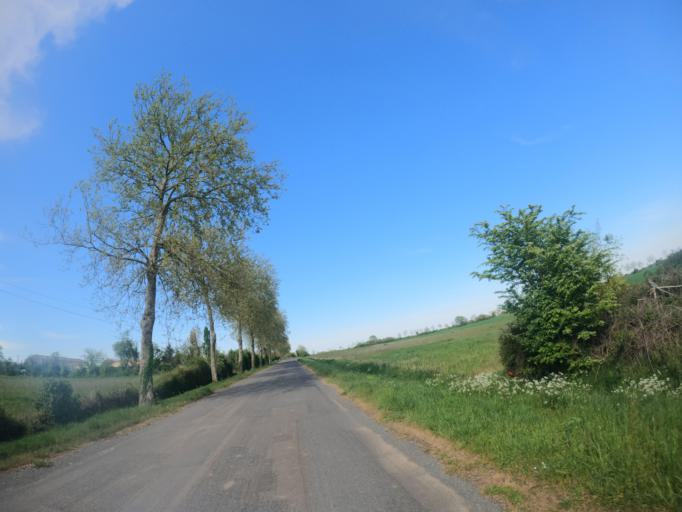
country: FR
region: Poitou-Charentes
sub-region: Departement des Deux-Sevres
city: Saint-Varent
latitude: 46.9031
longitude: -0.1938
